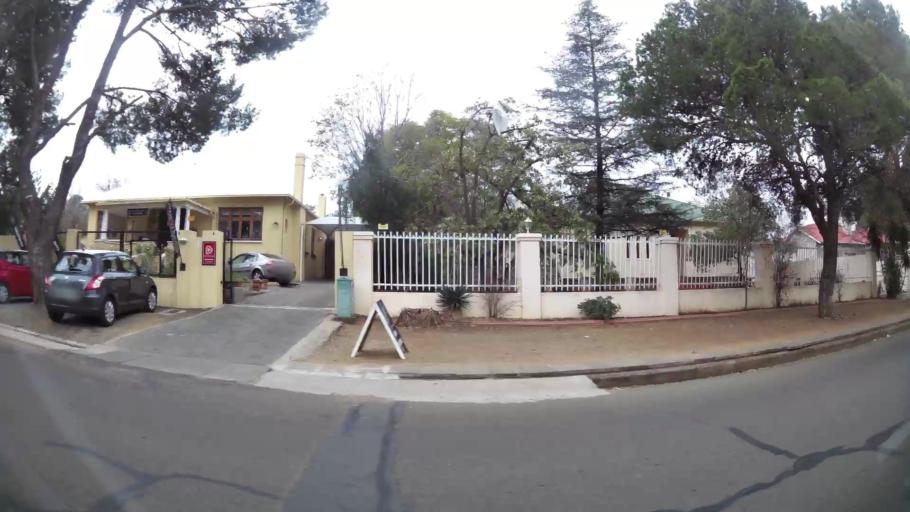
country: ZA
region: Orange Free State
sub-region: Mangaung Metropolitan Municipality
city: Bloemfontein
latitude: -29.1041
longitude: 26.2123
